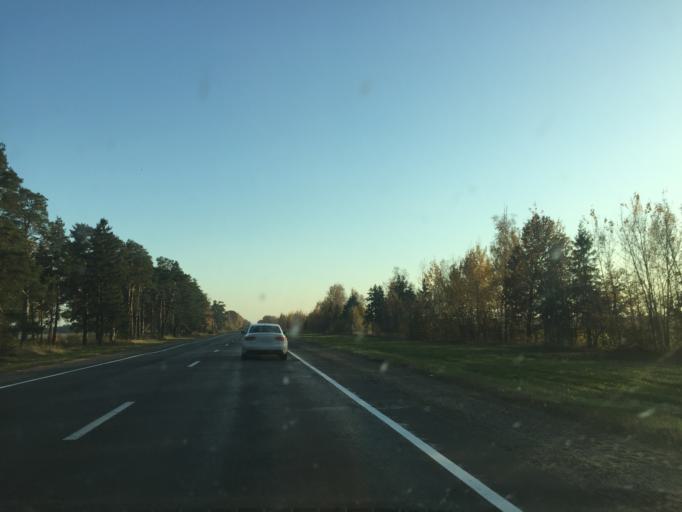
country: BY
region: Mogilev
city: Poselok Voskhod
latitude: 53.7450
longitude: 30.3658
